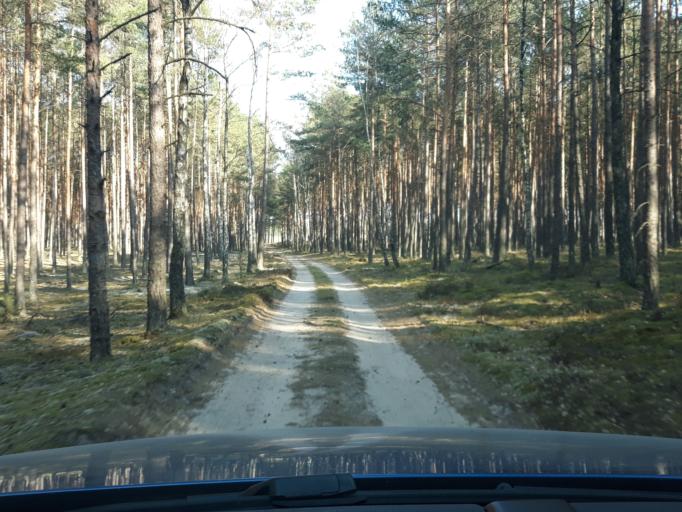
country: PL
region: Pomeranian Voivodeship
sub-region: Powiat bytowski
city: Lipnica
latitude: 53.9181
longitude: 17.4658
